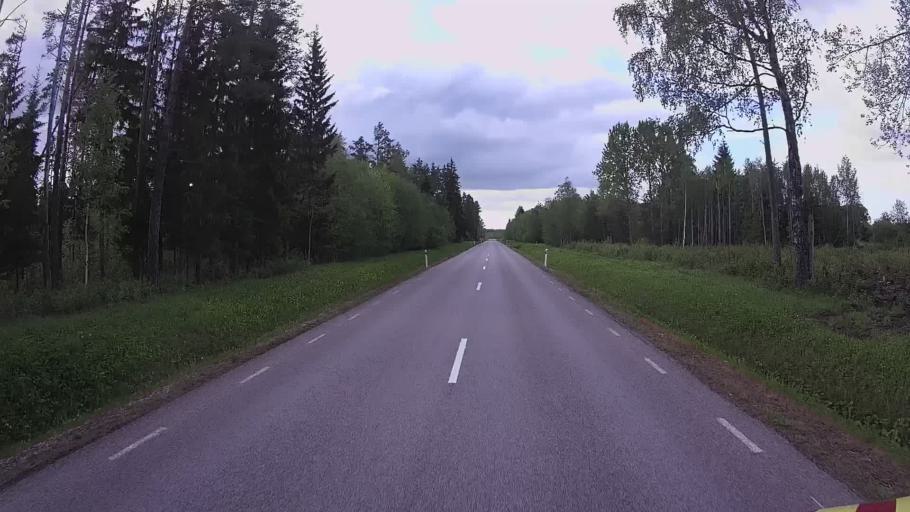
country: EE
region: Jogevamaa
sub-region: Mustvee linn
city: Mustvee
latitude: 59.0724
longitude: 26.9975
